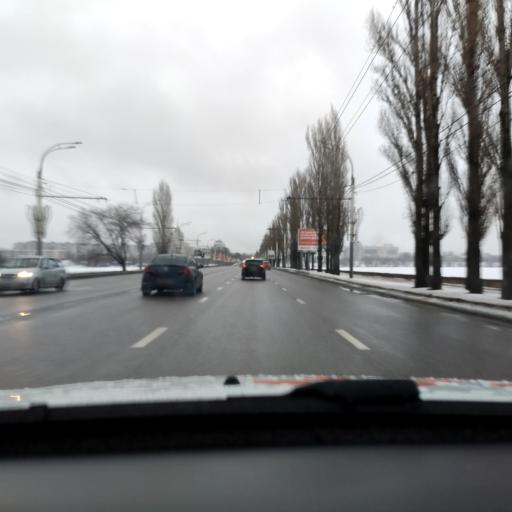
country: RU
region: Voronezj
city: Voronezh
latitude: 51.6673
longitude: 39.2323
